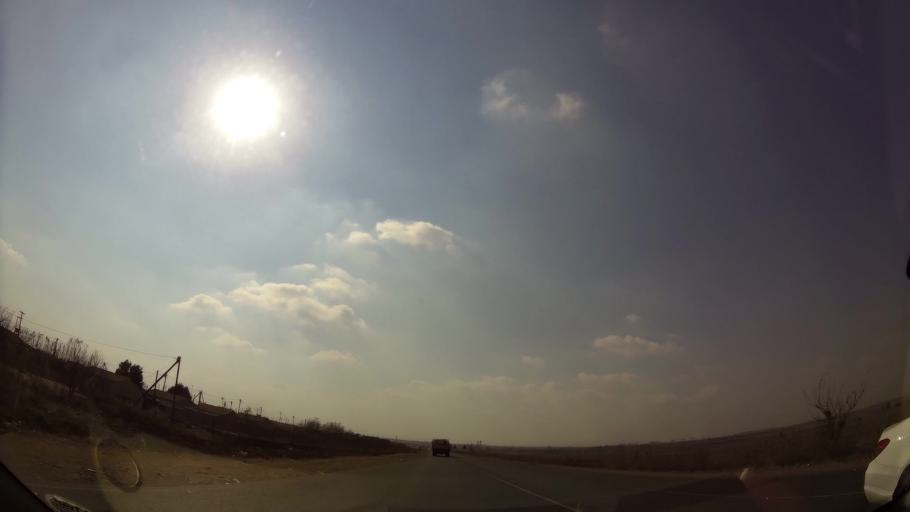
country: ZA
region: Gauteng
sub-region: Ekurhuleni Metropolitan Municipality
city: Springs
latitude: -26.1396
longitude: 28.4522
